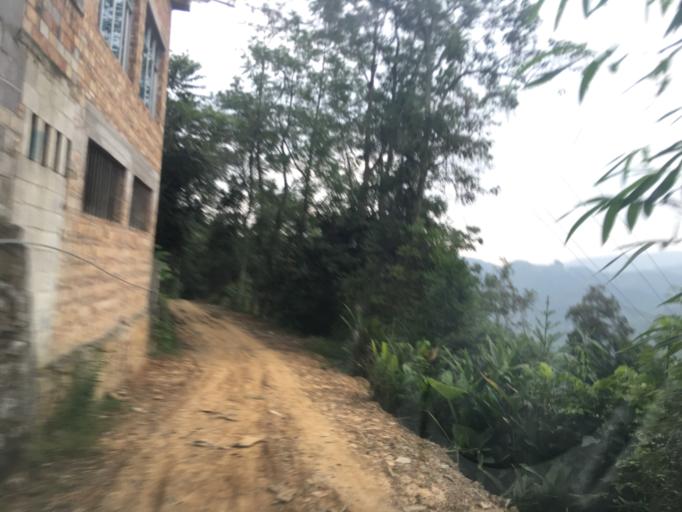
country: CN
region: Guangxi Zhuangzu Zizhiqu
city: Xinzhou
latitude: 25.1666
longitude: 105.6855
